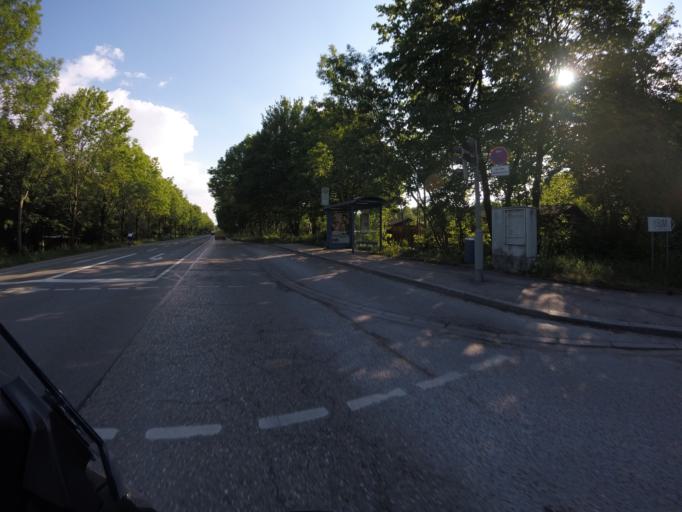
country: DE
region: Bavaria
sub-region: Upper Bavaria
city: Unterfoehring
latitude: 48.2040
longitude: 11.6295
